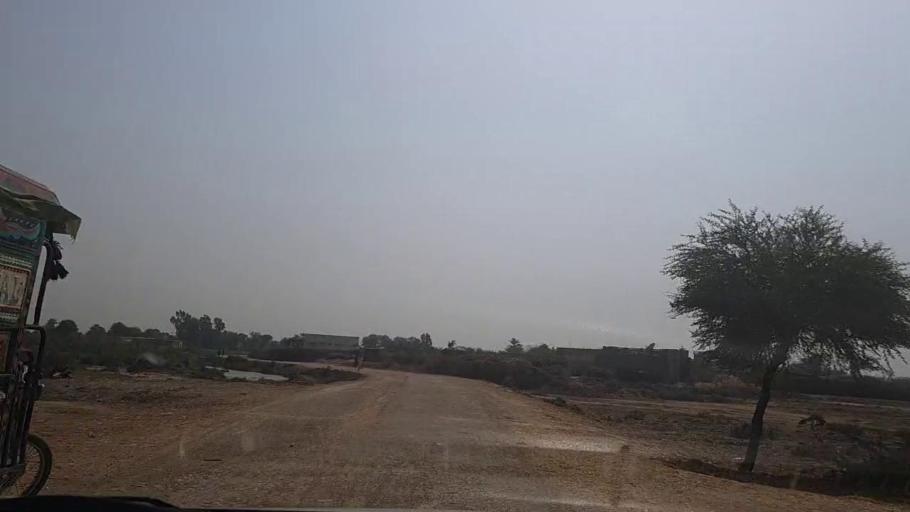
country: PK
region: Sindh
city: Pithoro
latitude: 25.5506
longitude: 69.2487
